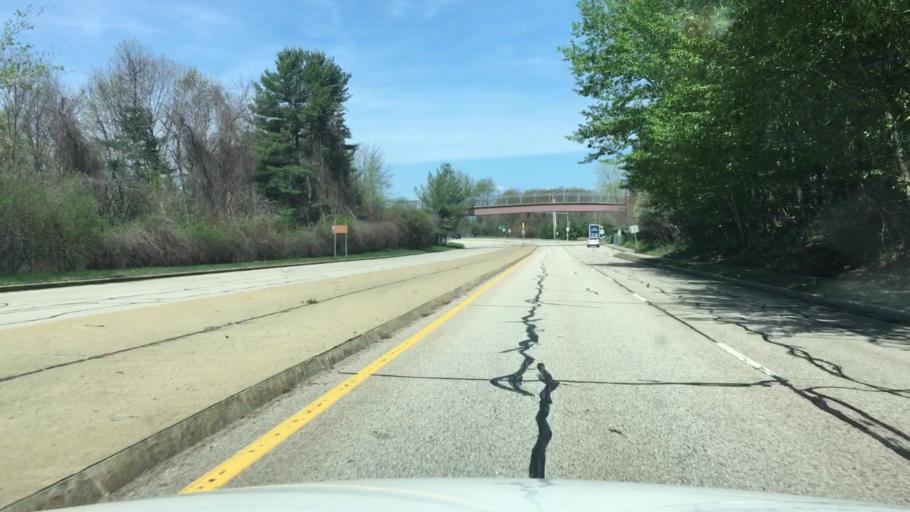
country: US
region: Maine
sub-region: York County
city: South Eliot
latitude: 43.0856
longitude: -70.7827
